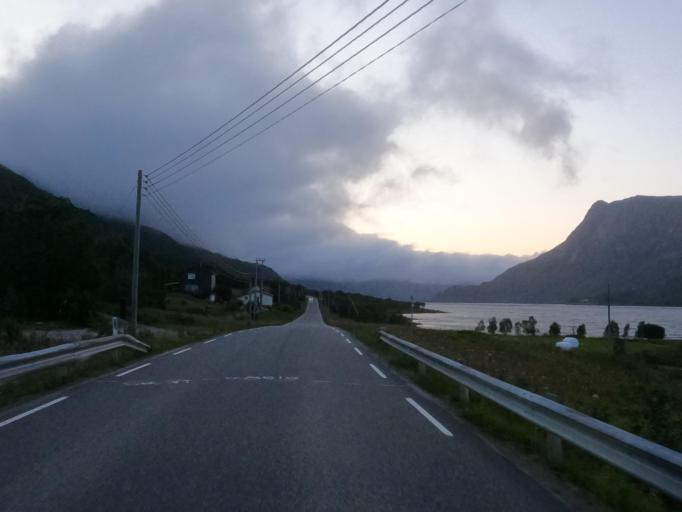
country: NO
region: Nordland
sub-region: Lodingen
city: Lodingen
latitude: 68.5711
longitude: 15.7959
